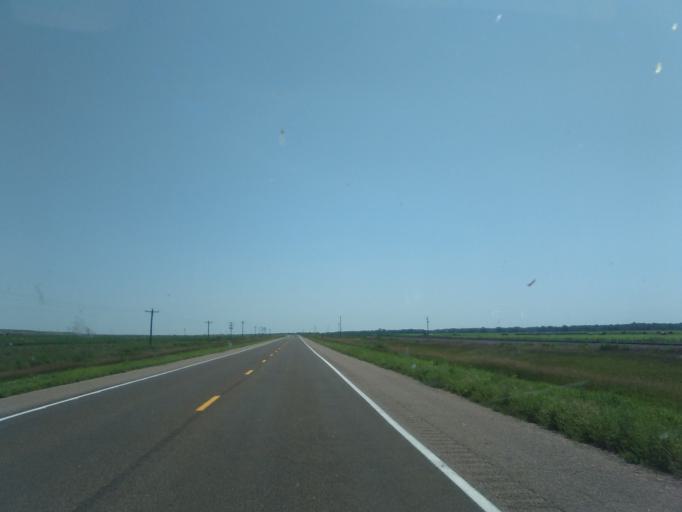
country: US
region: Nebraska
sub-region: Dundy County
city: Benkelman
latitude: 40.1282
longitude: -101.2961
